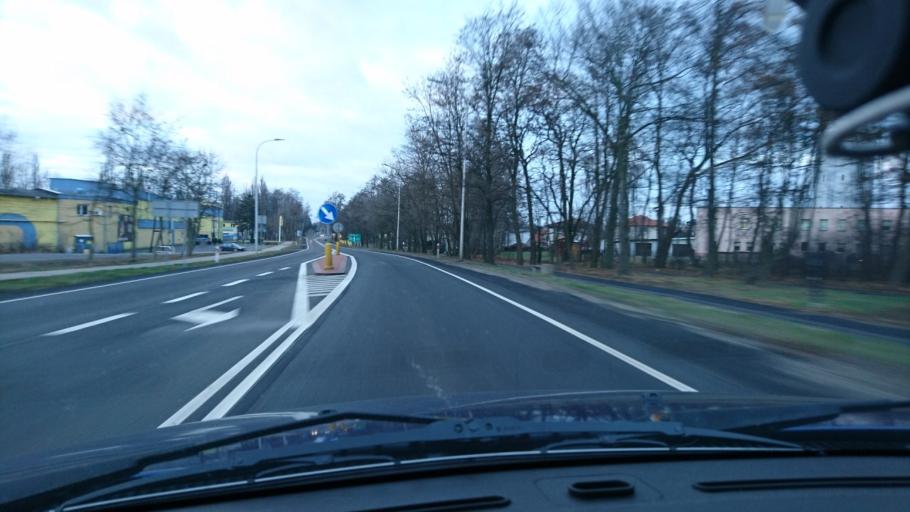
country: PL
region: Greater Poland Voivodeship
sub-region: Powiat ostrzeszowski
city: Ostrzeszow
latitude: 51.4183
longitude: 17.9306
